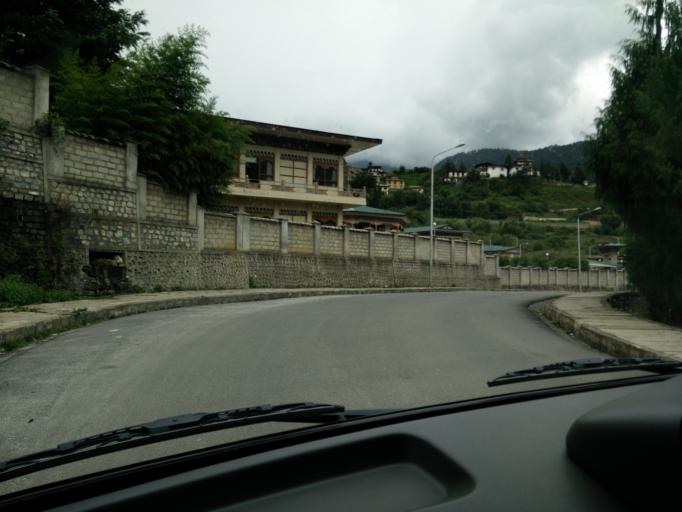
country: BT
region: Thimphu
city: Thimphu
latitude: 27.4707
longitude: 89.6319
